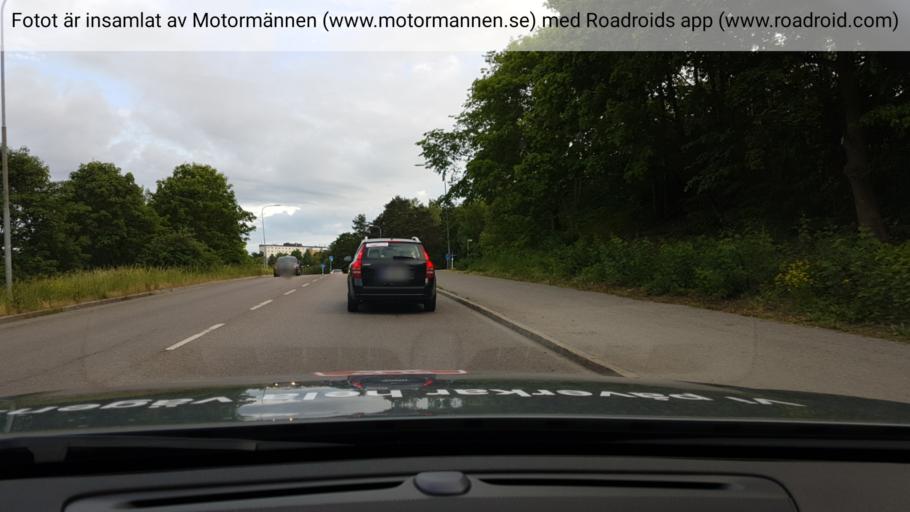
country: SE
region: Stockholm
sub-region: Stockholms Kommun
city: Arsta
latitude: 59.2916
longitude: 18.0371
